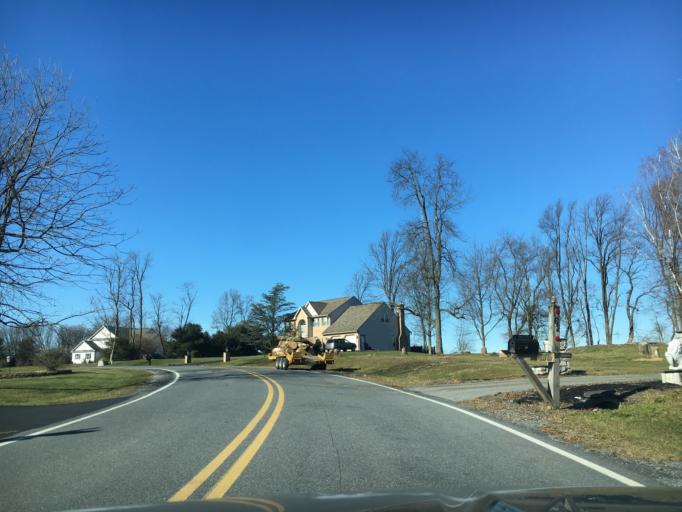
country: US
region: Pennsylvania
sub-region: Berks County
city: Fleetwood
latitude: 40.4276
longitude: -75.8282
